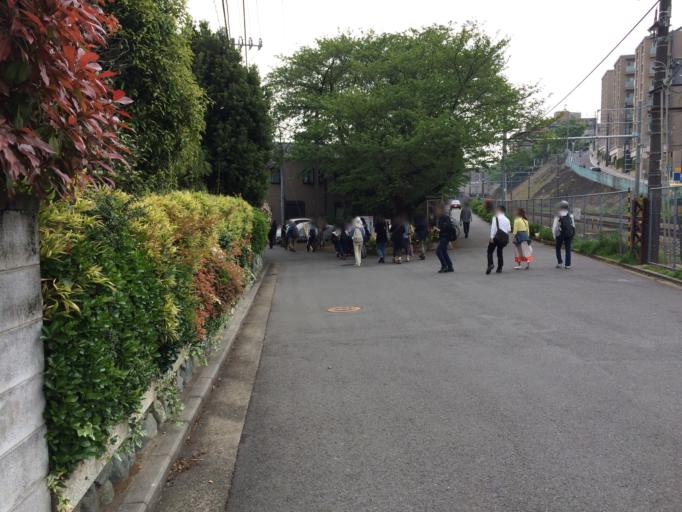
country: JP
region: Kanagawa
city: Yokohama
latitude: 35.5083
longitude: 139.6356
